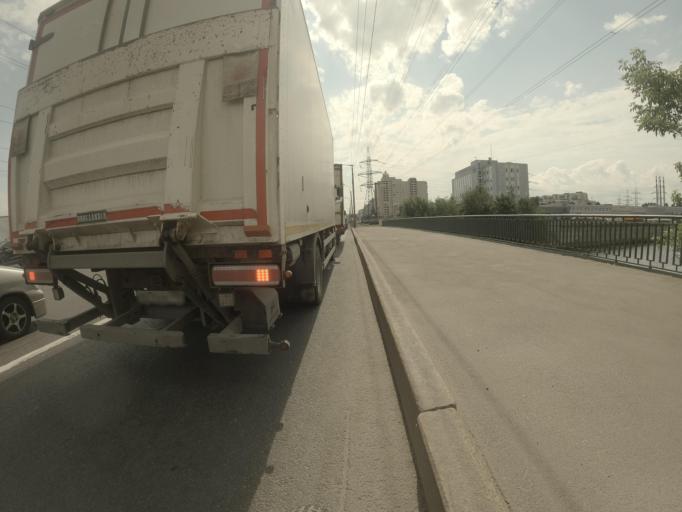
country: RU
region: St.-Petersburg
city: Krasnogvargeisky
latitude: 59.9585
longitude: 30.4640
